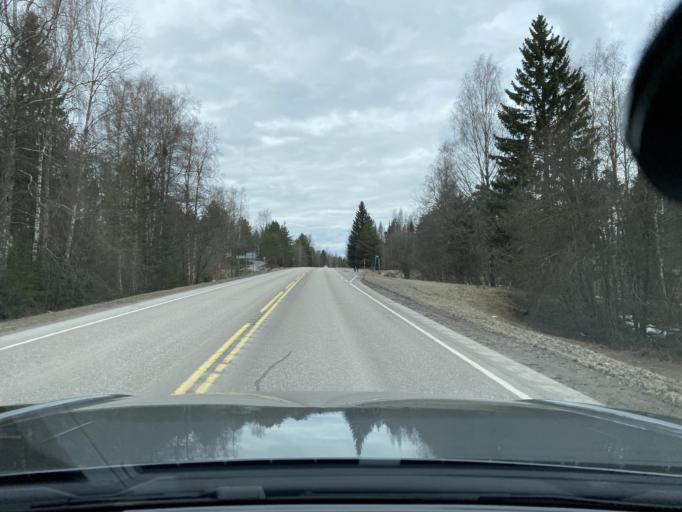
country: FI
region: Haeme
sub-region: Riihimaeki
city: Riihimaeki
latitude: 60.7024
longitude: 24.7407
